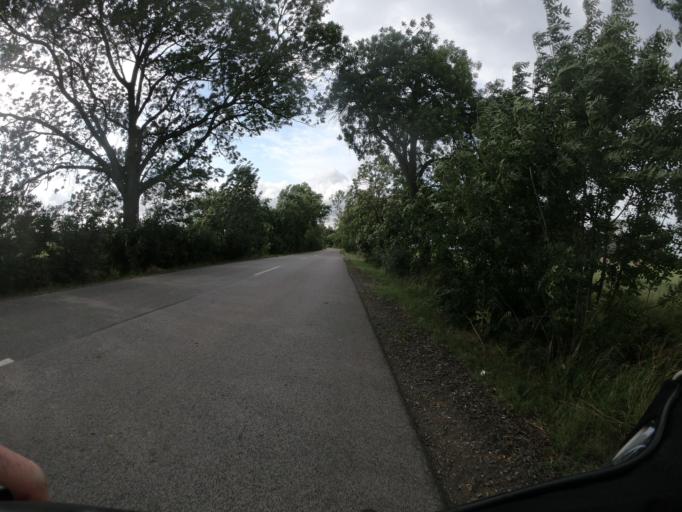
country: HU
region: Borsod-Abauj-Zemplen
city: Mezocsat
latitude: 47.8240
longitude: 20.8503
